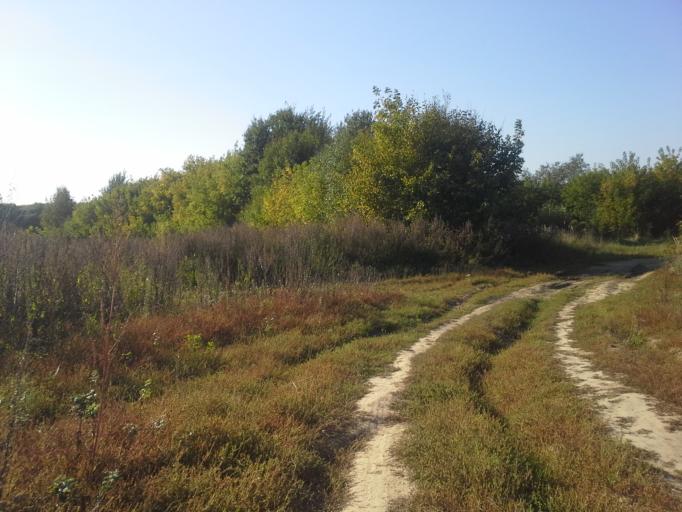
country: RU
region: Moskovskaya
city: Kommunarka
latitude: 55.5560
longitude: 37.4465
